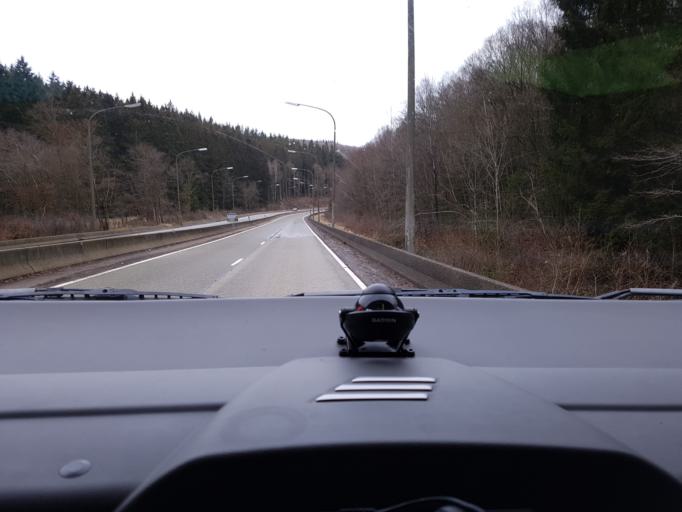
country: BE
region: Wallonia
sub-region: Province du Luxembourg
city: Tenneville
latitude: 50.1284
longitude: 5.4551
